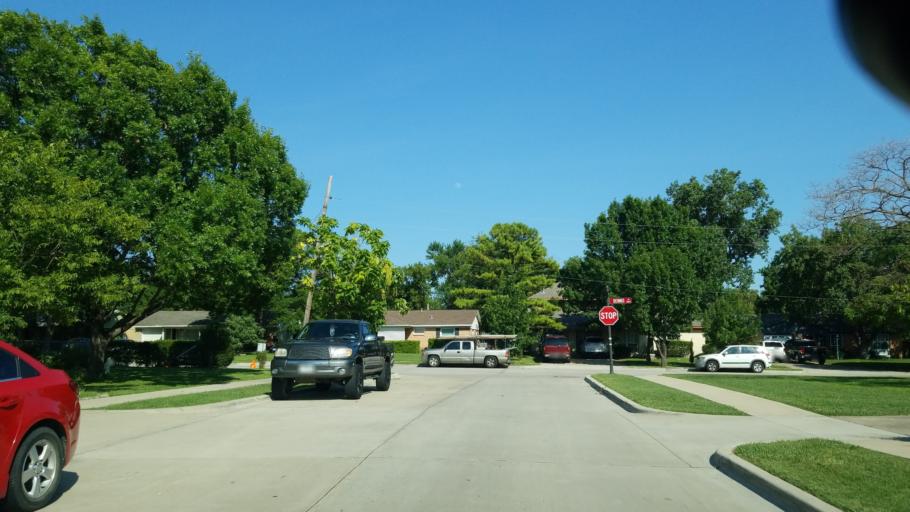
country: US
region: Texas
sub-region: Dallas County
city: Farmers Branch
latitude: 32.9324
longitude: -96.8899
